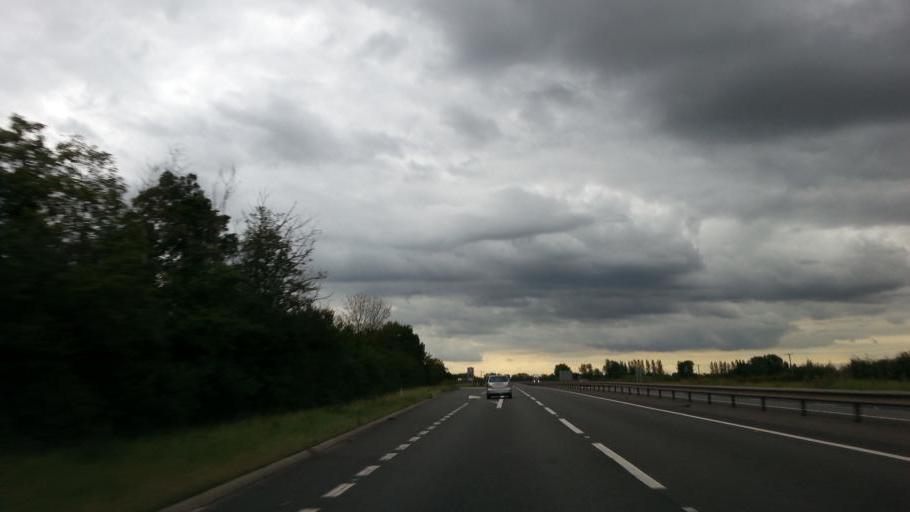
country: GB
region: England
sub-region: Nottinghamshire
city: South Collingham
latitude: 53.1604
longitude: -0.8073
